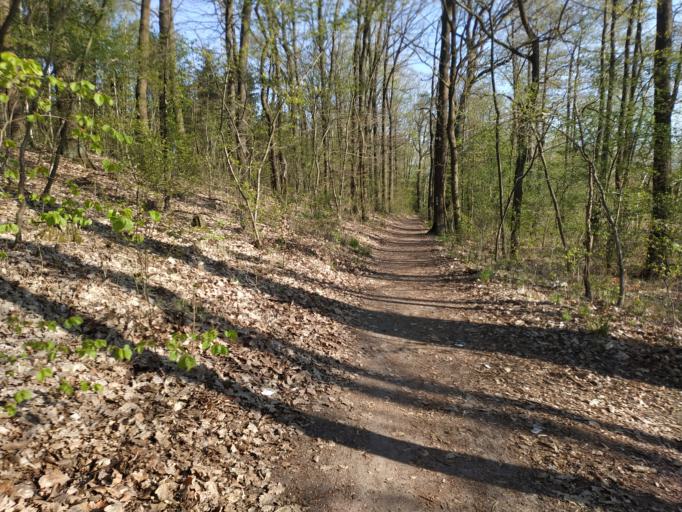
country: DE
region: Brandenburg
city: Strausberg
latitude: 52.5657
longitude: 13.8359
